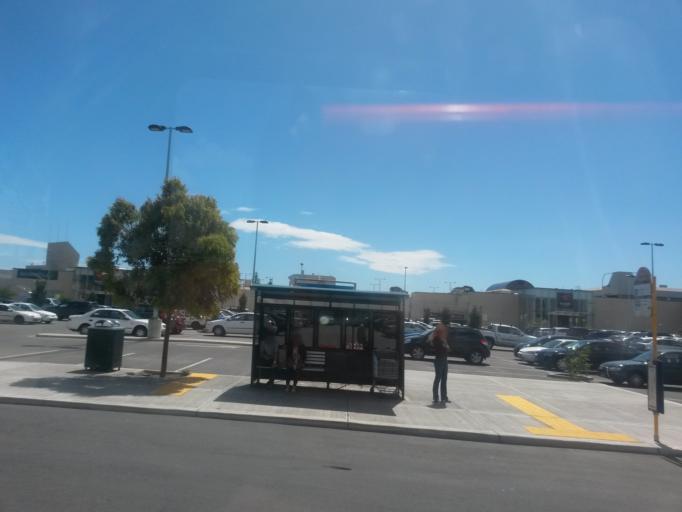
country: AU
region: South Australia
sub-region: Charles Sturt
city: Woodville North
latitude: -34.8735
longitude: 138.5513
